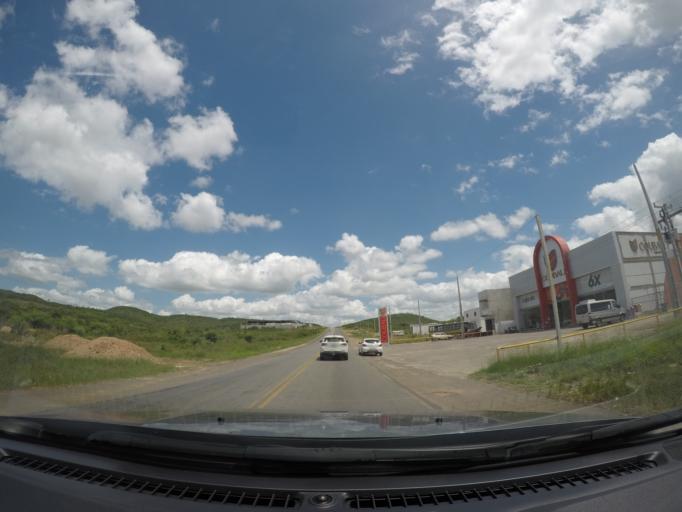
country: BR
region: Bahia
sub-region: Ipira
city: Ipira
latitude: -12.1671
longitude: -39.7351
